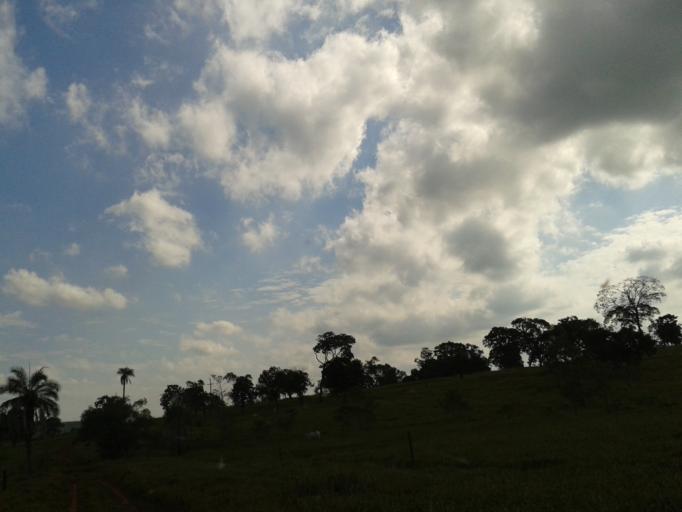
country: BR
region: Minas Gerais
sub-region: Campina Verde
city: Campina Verde
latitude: -19.3930
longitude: -49.6856
